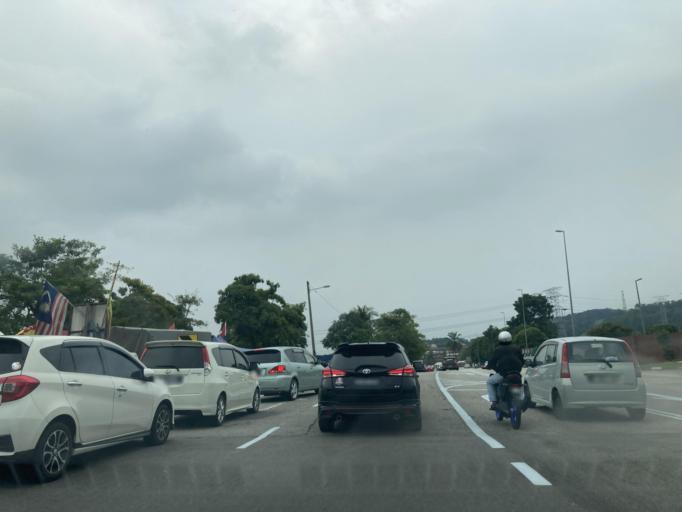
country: MY
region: Selangor
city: Kampung Baru Subang
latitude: 3.2015
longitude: 101.5472
